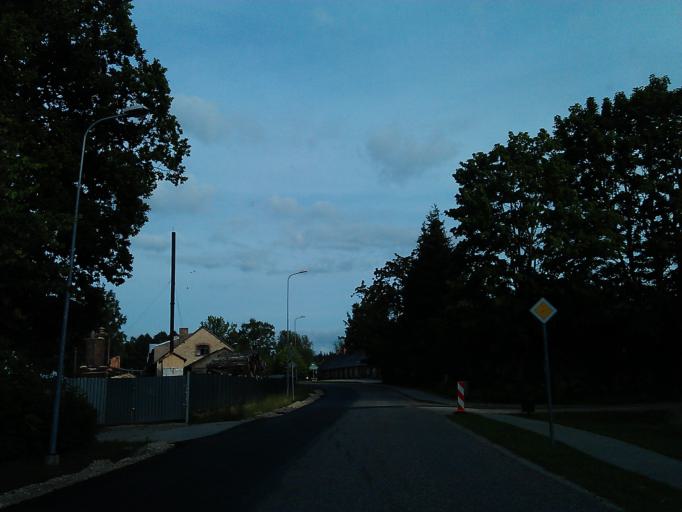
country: LV
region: Amatas Novads
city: Drabesi
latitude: 57.2029
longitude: 25.1687
